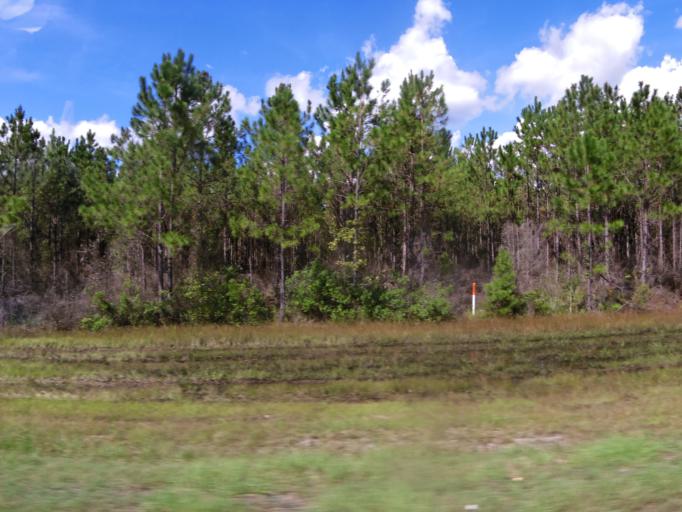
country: US
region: Florida
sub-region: Hamilton County
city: Jasper
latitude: 30.6800
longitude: -82.6019
